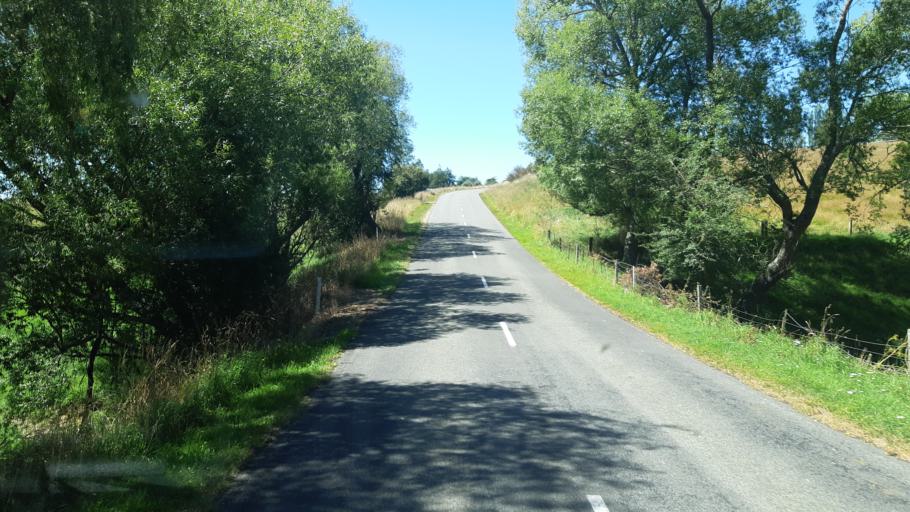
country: NZ
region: Canterbury
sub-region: Timaru District
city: Timaru
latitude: -44.4065
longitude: 171.1479
